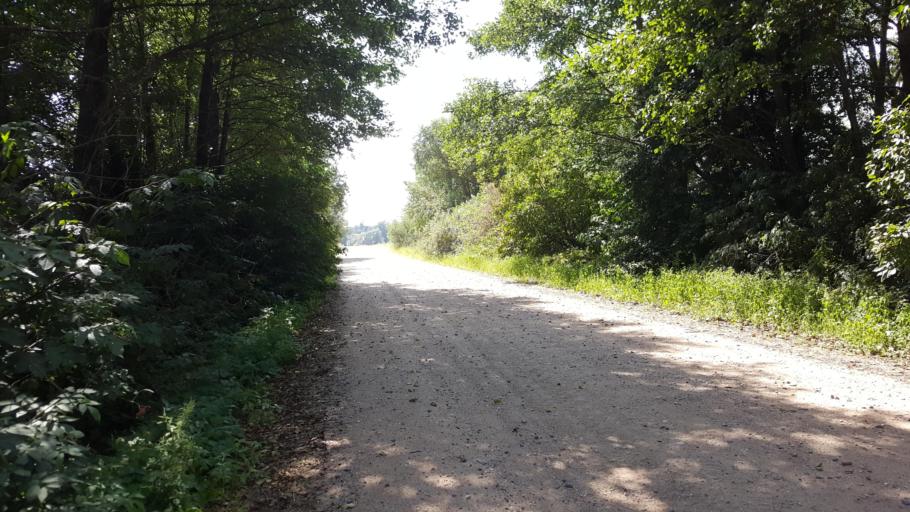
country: PL
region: Podlasie
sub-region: Powiat hajnowski
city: Czeremcha
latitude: 52.5471
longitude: 23.5462
